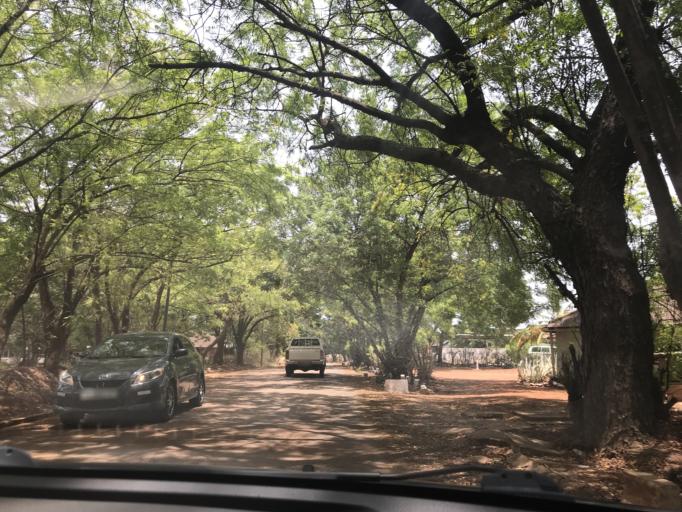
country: GH
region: Greater Accra
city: Teshi Old Town
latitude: 5.5824
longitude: -0.1559
